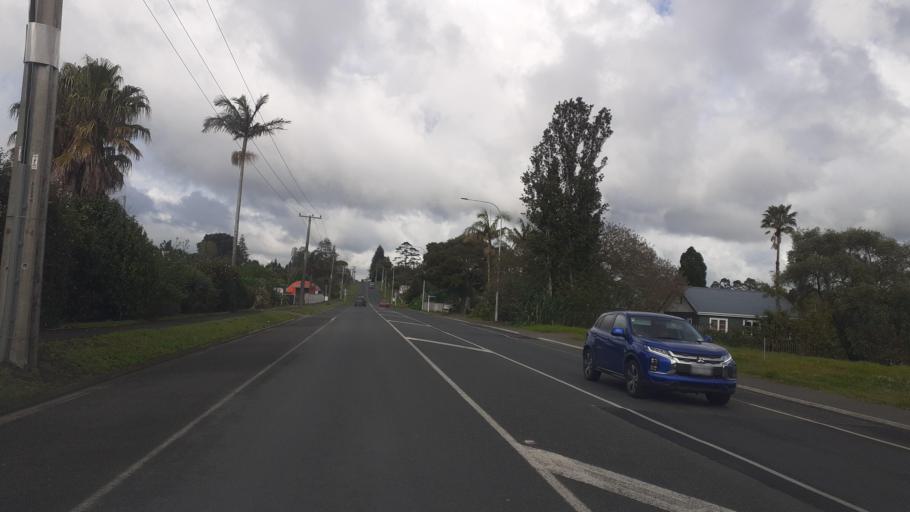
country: NZ
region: Northland
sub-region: Far North District
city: Kerikeri
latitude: -35.2342
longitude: 173.9432
